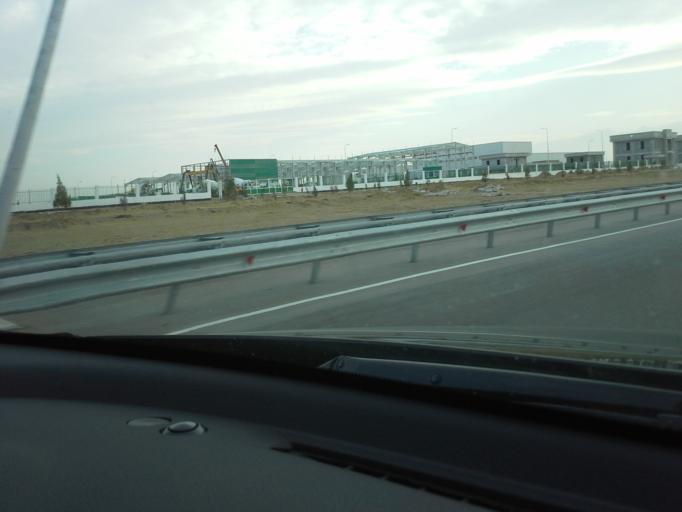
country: TM
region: Ahal
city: Abadan
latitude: 38.0661
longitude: 58.3118
